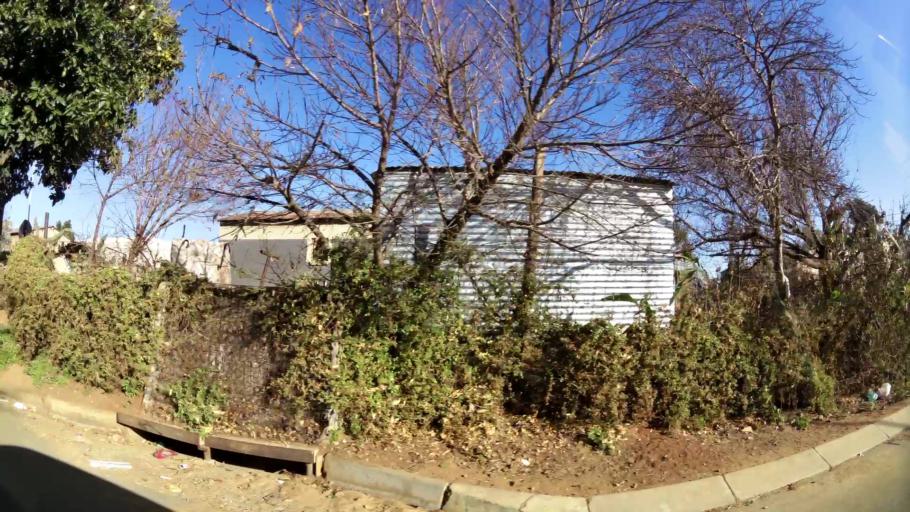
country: ZA
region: Gauteng
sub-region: Ekurhuleni Metropolitan Municipality
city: Tembisa
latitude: -26.0227
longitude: 28.2181
